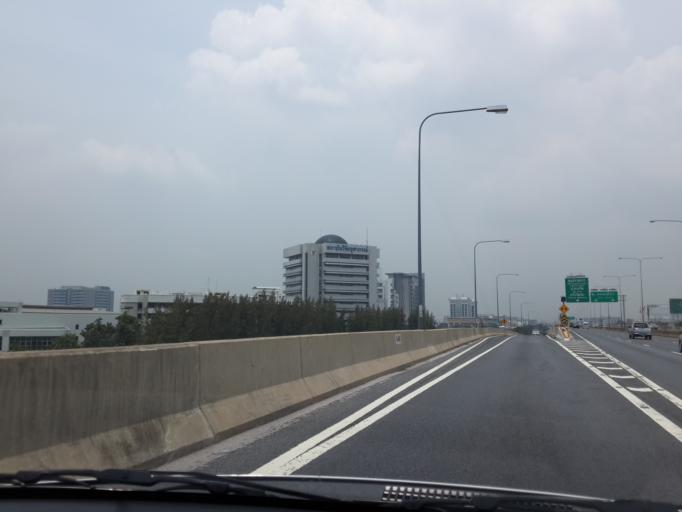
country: TH
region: Bangkok
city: Lak Si
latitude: 13.8767
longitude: 100.5772
